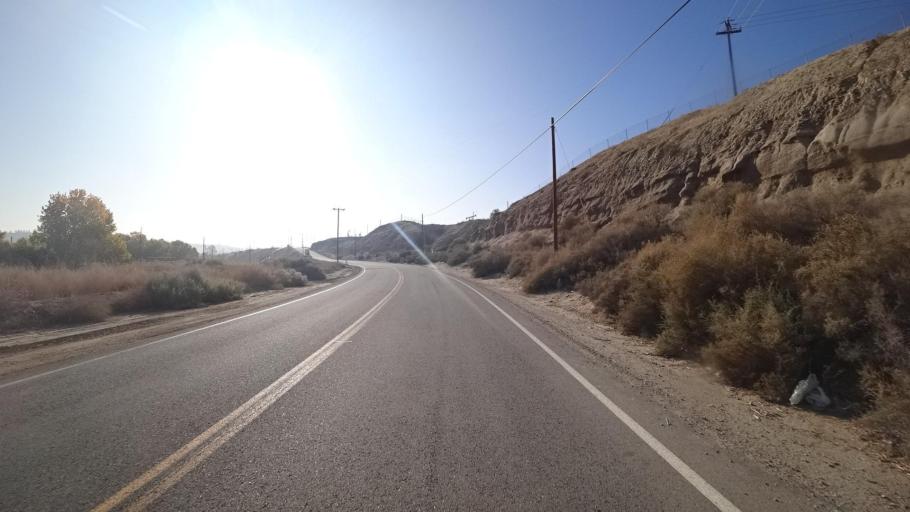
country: US
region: California
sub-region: Kern County
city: Oildale
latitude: 35.4344
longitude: -118.9507
